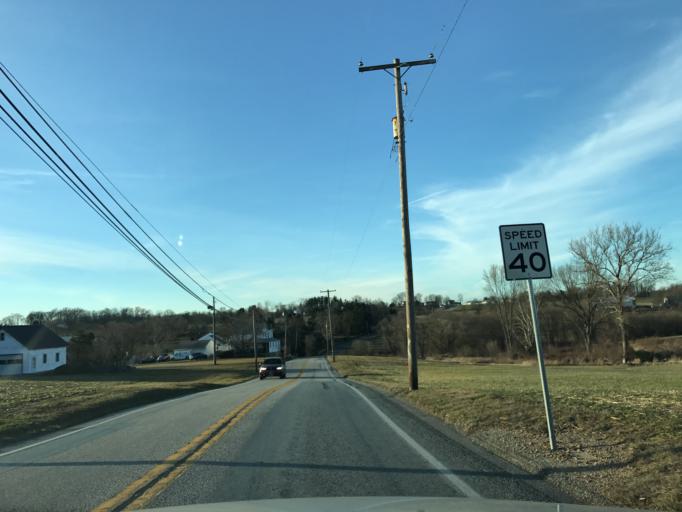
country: US
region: Pennsylvania
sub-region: Lancaster County
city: Elizabethtown
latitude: 40.1294
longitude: -76.5964
